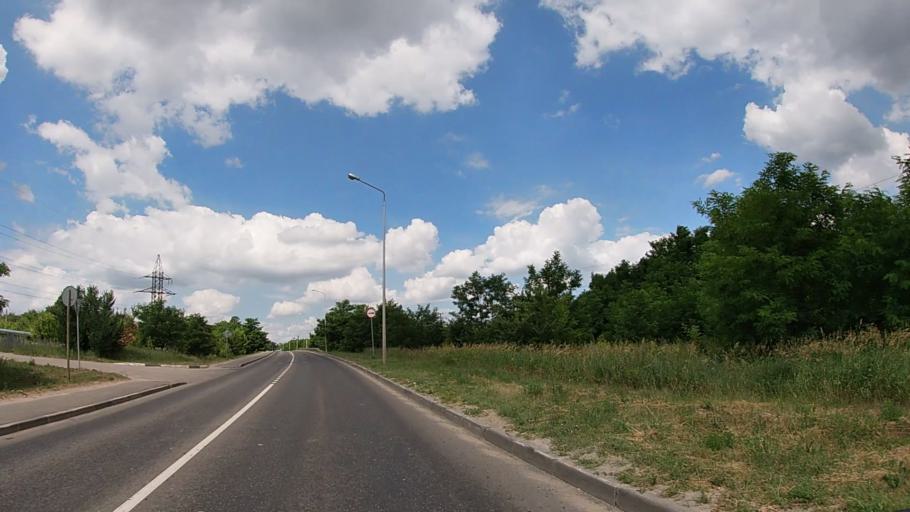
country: RU
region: Belgorod
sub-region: Belgorodskiy Rayon
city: Belgorod
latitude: 50.5937
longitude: 36.5588
